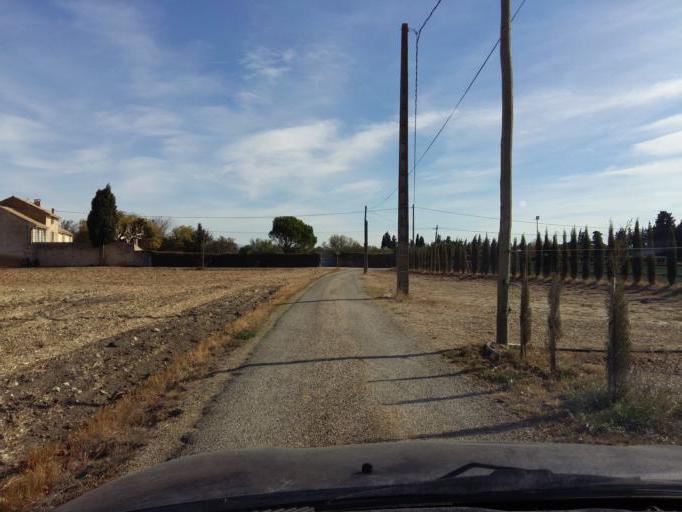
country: FR
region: Provence-Alpes-Cote d'Azur
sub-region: Departement du Vaucluse
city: Serignan-du-Comtat
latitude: 44.1705
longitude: 4.8416
